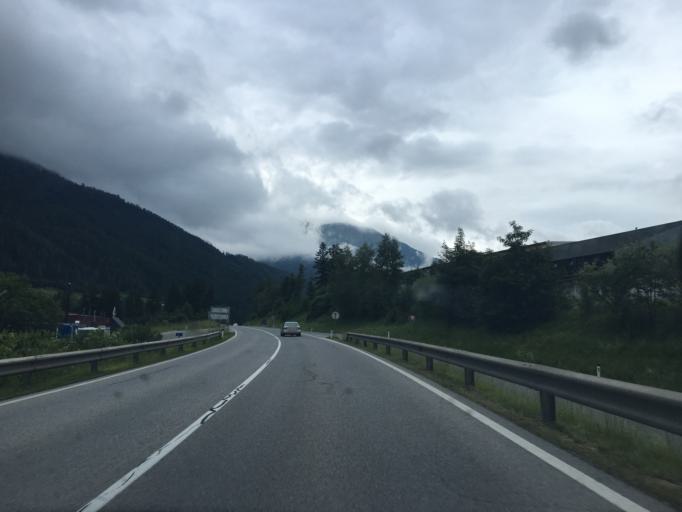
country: AT
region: Tyrol
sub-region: Politischer Bezirk Innsbruck Land
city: Neustift im Stubaital
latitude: 47.1331
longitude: 11.3411
